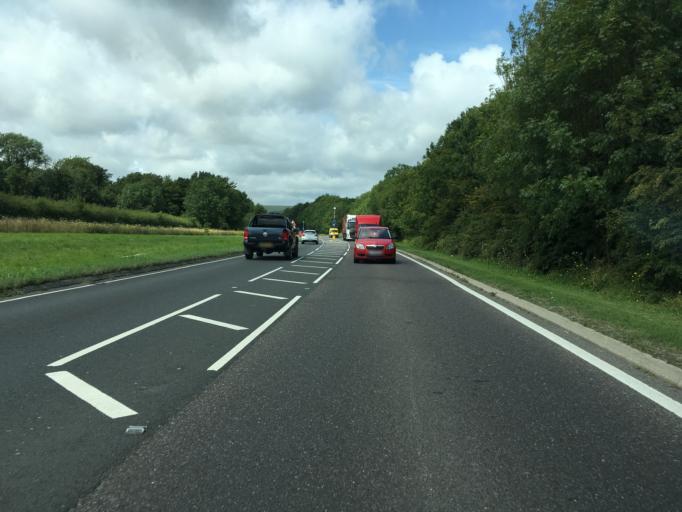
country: GB
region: England
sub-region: East Sussex
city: Ringmer
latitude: 50.8519
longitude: 0.1096
